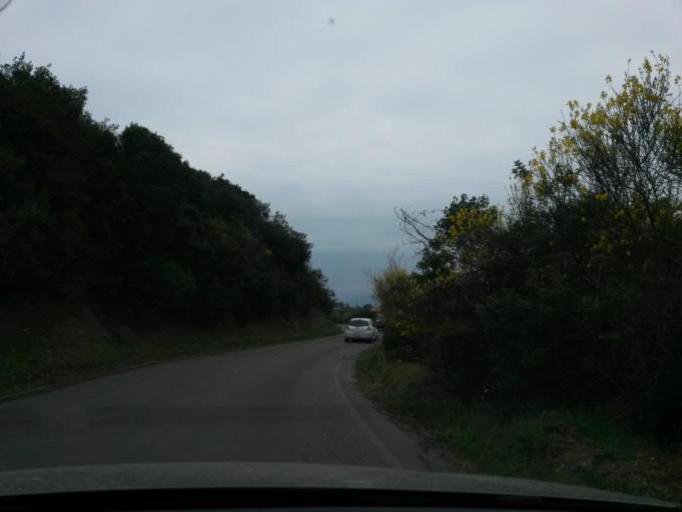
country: IT
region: Tuscany
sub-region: Provincia di Livorno
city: Capoliveri
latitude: 42.7325
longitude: 10.3787
